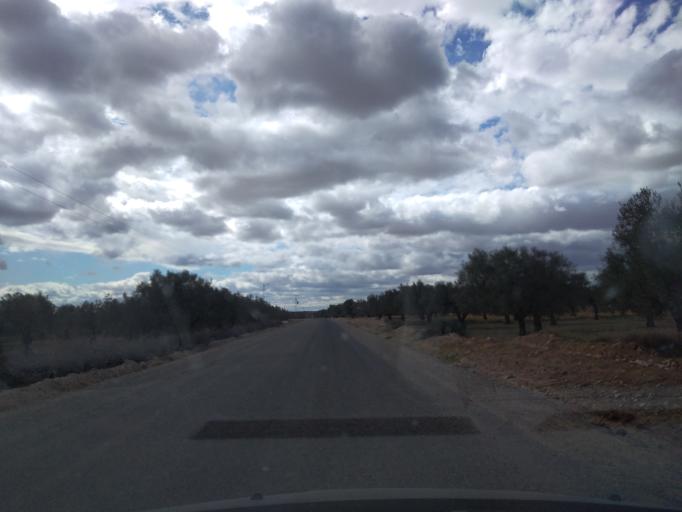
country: TN
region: Susah
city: Akouda
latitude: 35.8116
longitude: 10.4451
